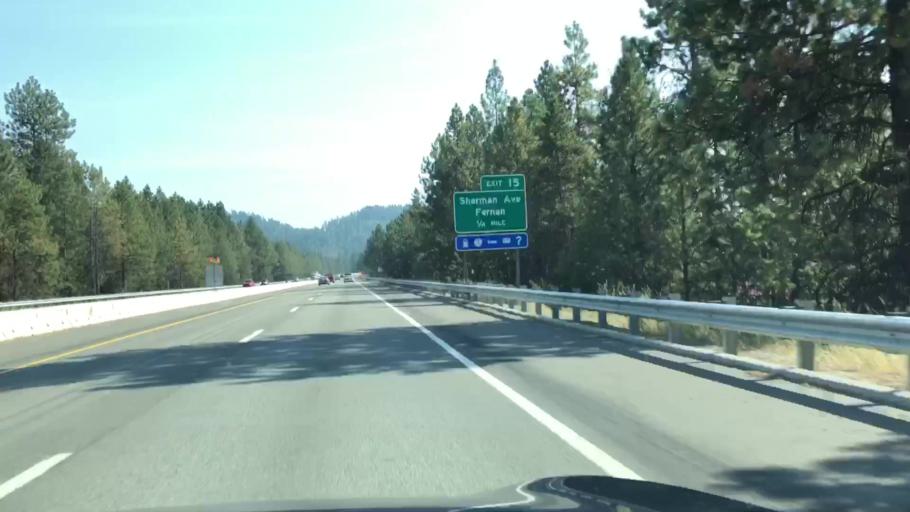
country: US
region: Idaho
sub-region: Kootenai County
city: Coeur d'Alene
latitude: 47.6820
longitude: -116.7584
